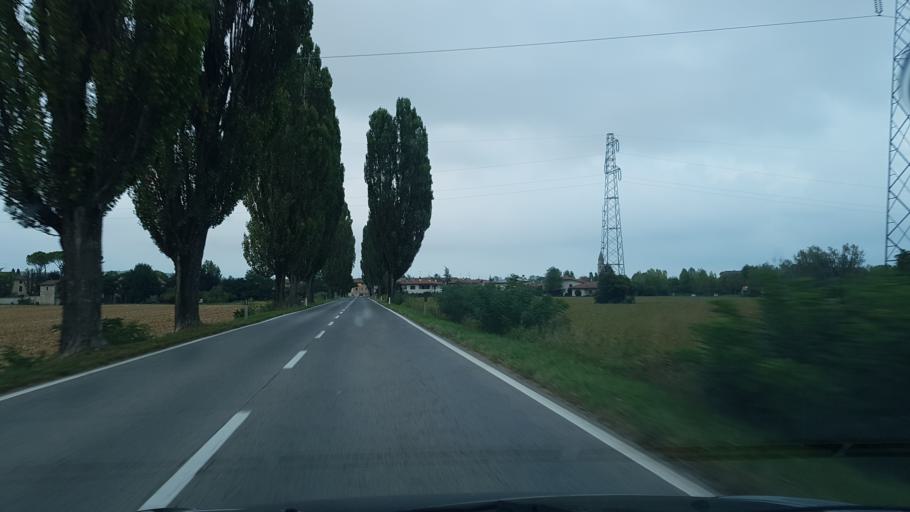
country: IT
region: Friuli Venezia Giulia
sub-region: Provincia di Gorizia
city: Medea
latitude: 45.8974
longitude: 13.4125
